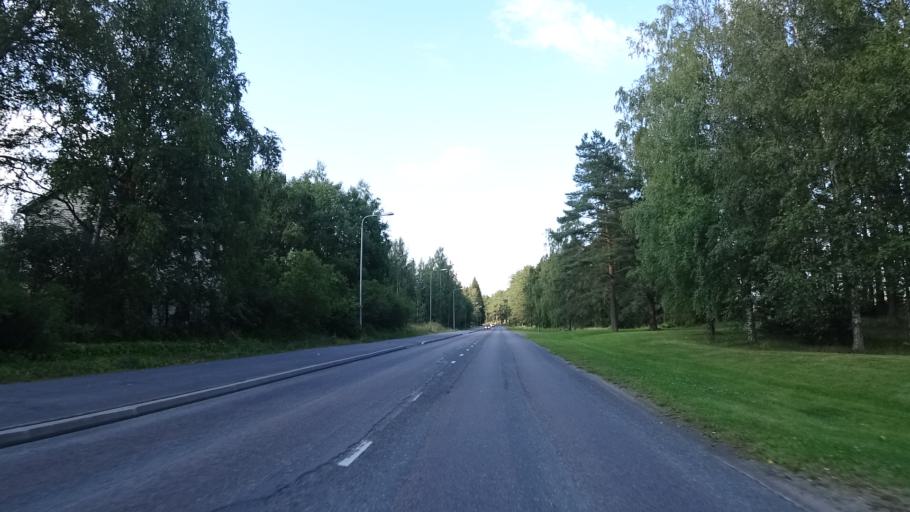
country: FI
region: South Karelia
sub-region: Imatra
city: Imatra
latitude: 61.1763
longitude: 28.7786
